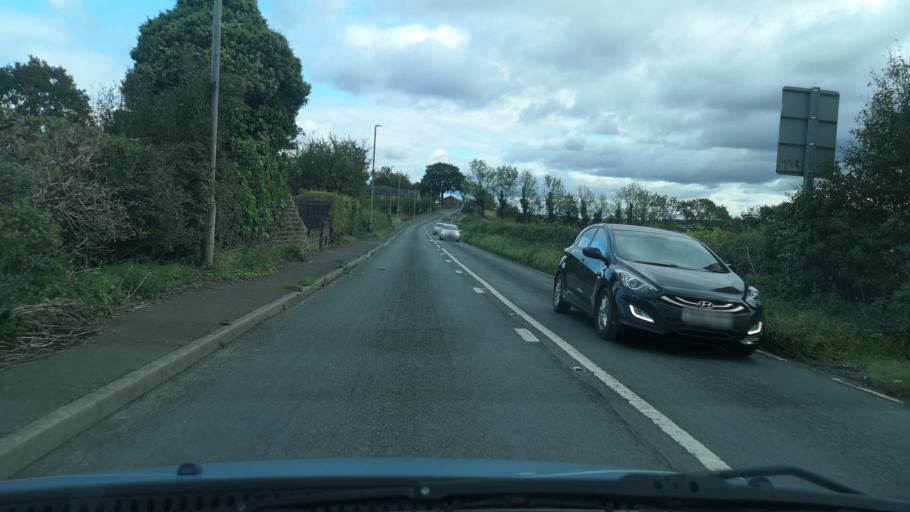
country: GB
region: England
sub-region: City and Borough of Wakefield
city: Middlestown
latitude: 53.6617
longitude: -1.5970
